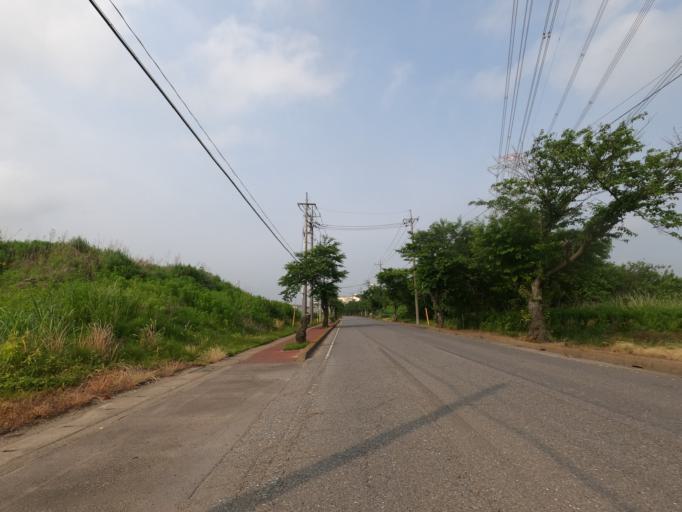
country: JP
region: Ibaraki
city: Moriya
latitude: 35.9552
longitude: 139.9520
